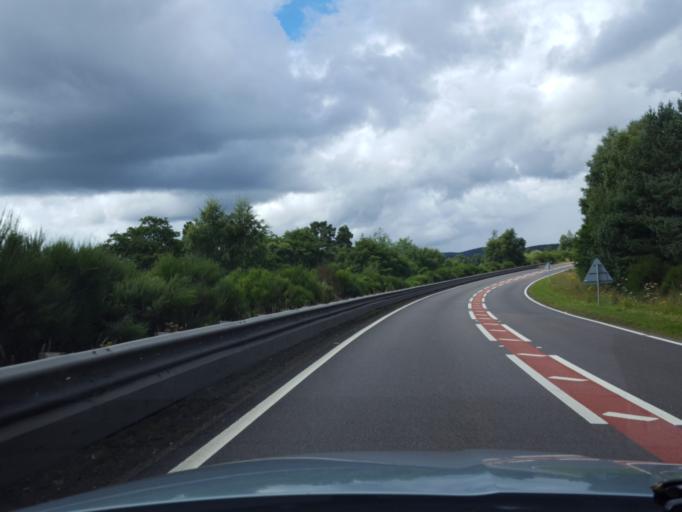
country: GB
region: Scotland
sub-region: Highland
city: Grantown on Spey
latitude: 57.2812
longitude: -3.6733
